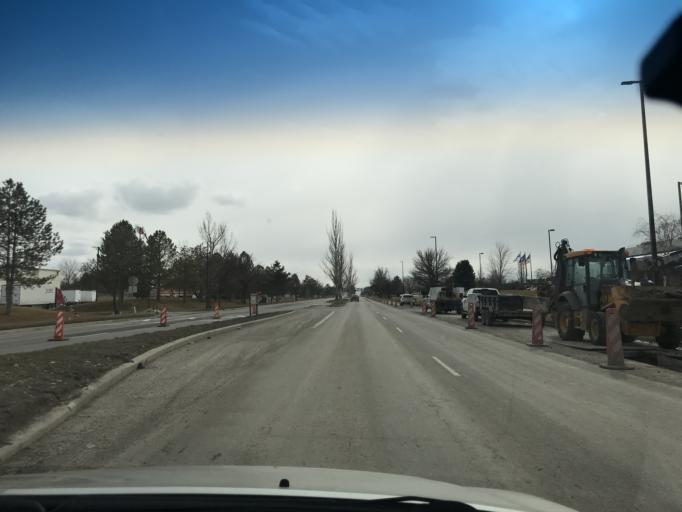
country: US
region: Utah
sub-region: Salt Lake County
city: West Valley City
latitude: 40.7800
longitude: -112.0252
